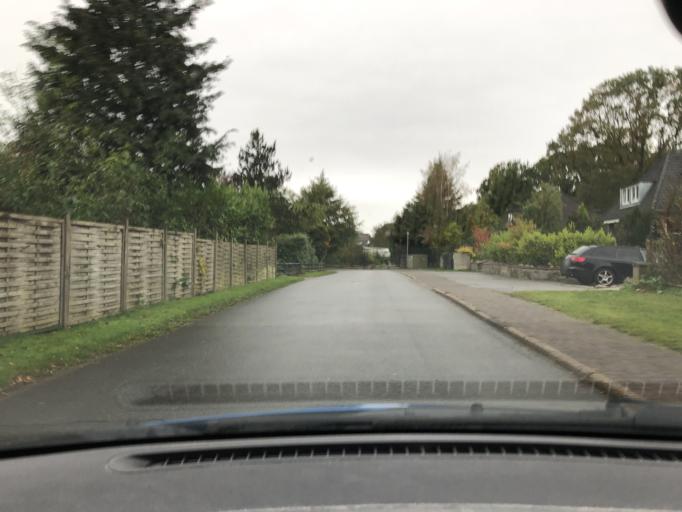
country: DE
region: Schleswig-Holstein
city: Fahrdorf
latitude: 54.5020
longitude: 9.6066
